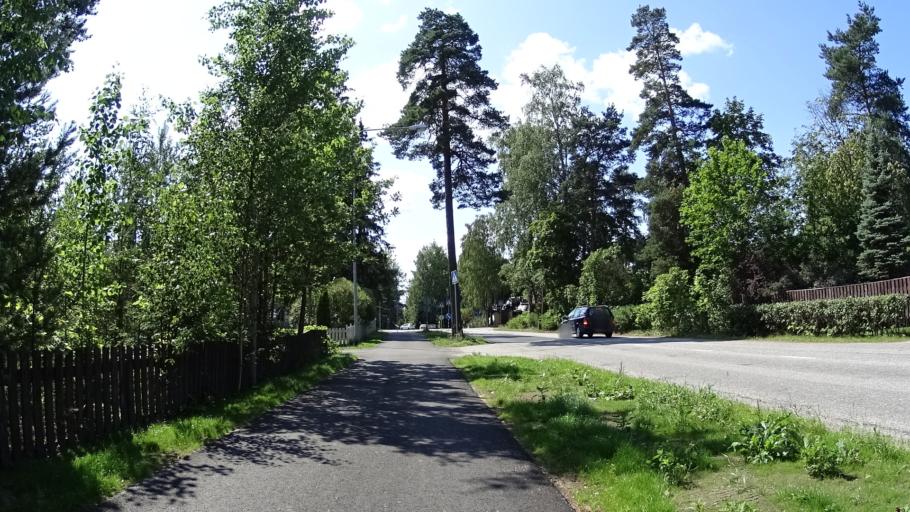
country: FI
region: Uusimaa
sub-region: Helsinki
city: Tuusula
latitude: 60.4068
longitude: 25.0130
